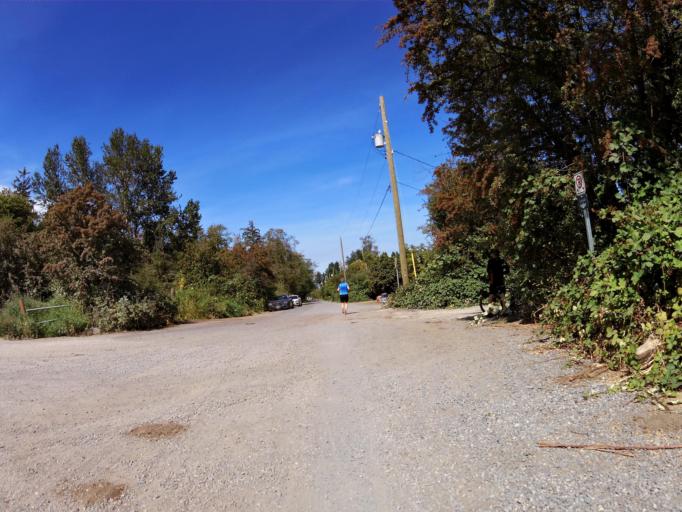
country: CA
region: British Columbia
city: North Saanich
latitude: 48.5578
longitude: -123.3871
